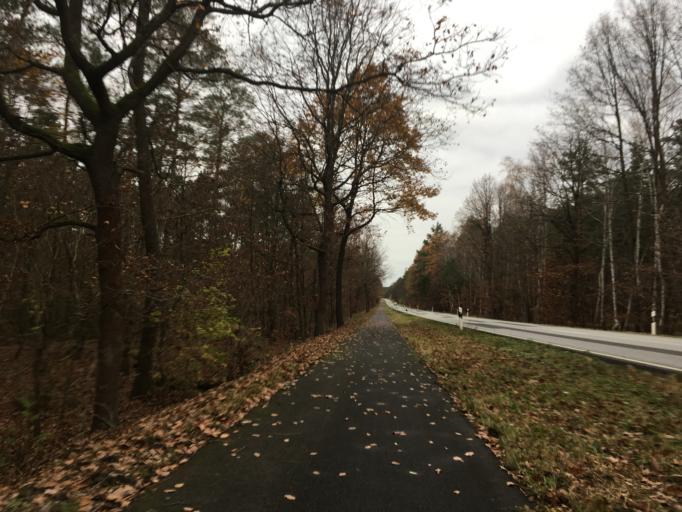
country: DE
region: Brandenburg
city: Mullrose
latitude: 52.2082
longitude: 14.4535
